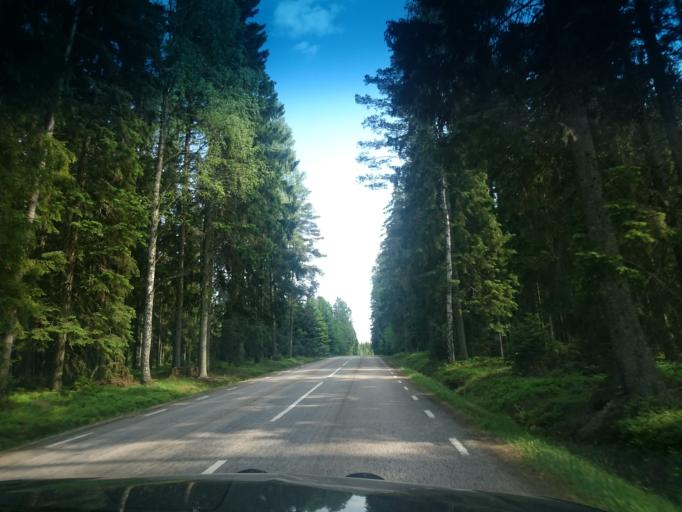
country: SE
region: Joenkoeping
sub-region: Vetlanda Kommun
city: Vetlanda
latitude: 57.3603
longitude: 15.0690
